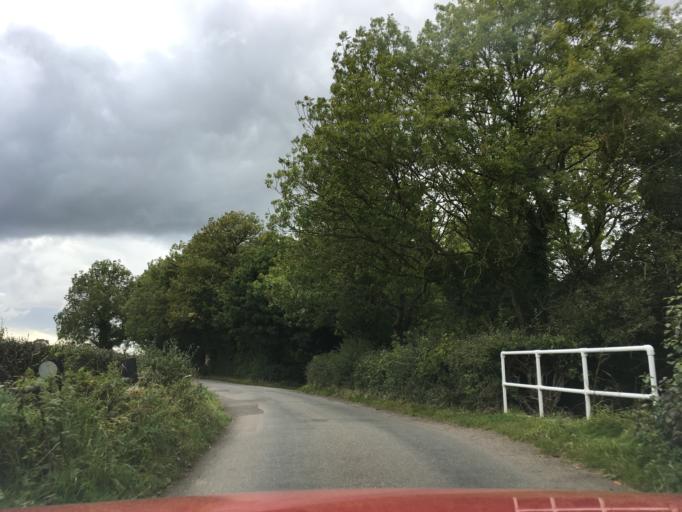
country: GB
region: England
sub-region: South Gloucestershire
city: Wickwar
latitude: 51.5966
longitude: -2.4257
